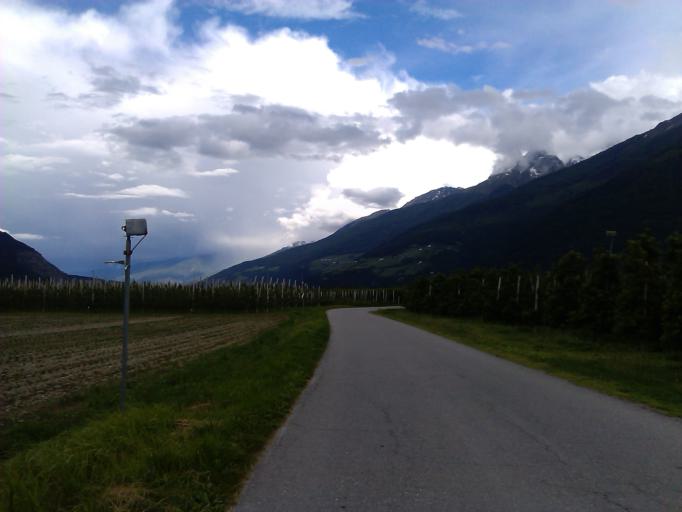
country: IT
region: Trentino-Alto Adige
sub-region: Bolzano
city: Prato Allo Stelvio
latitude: 46.6274
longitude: 10.6199
